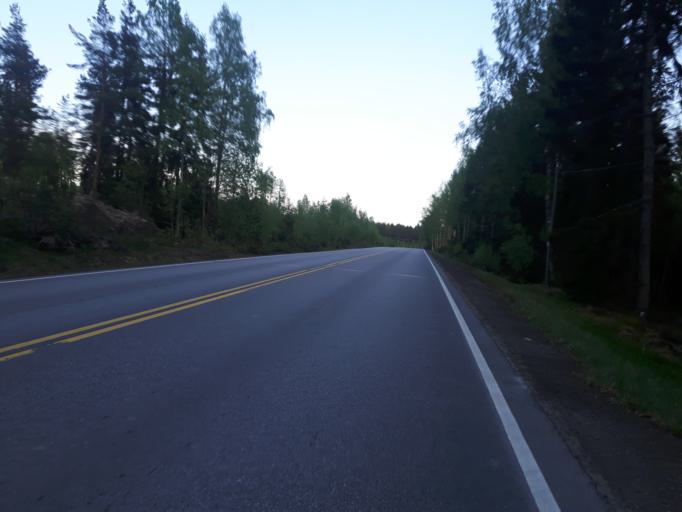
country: FI
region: Uusimaa
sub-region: Loviisa
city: Perna
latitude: 60.4566
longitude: 26.0821
